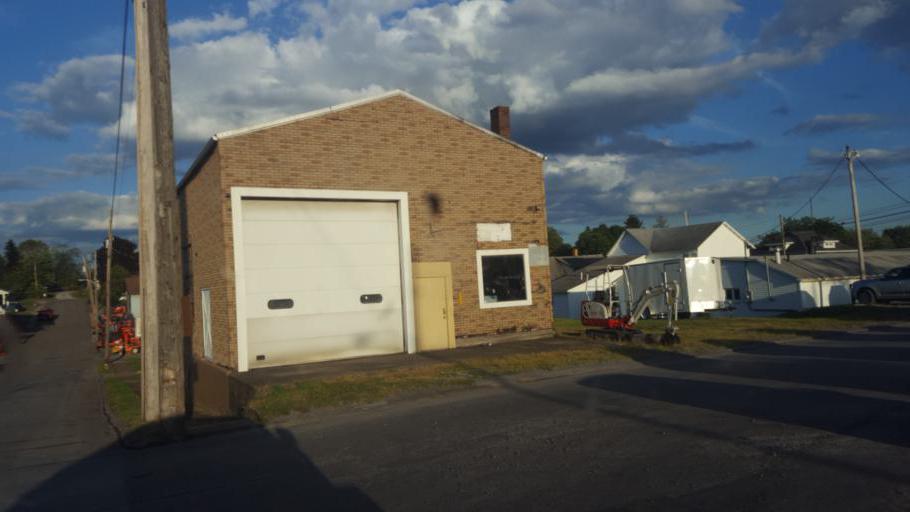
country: US
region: Pennsylvania
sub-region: Clarion County
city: Knox
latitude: 41.2363
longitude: -79.5358
